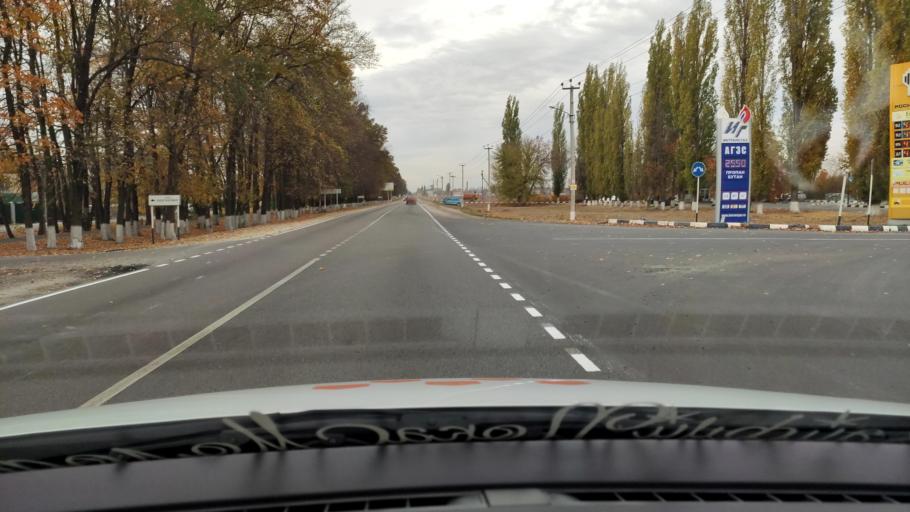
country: RU
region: Voronezj
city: Ramon'
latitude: 51.9121
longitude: 39.3235
